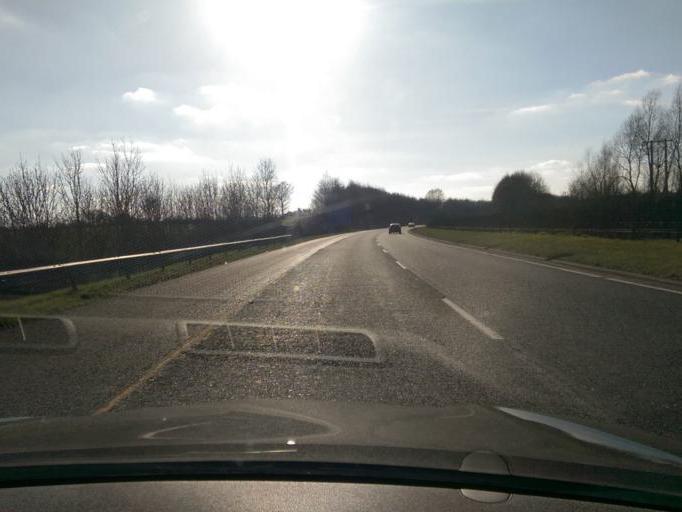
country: IE
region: Leinster
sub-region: Kildare
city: Athgarvan
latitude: 53.1611
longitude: -6.7840
